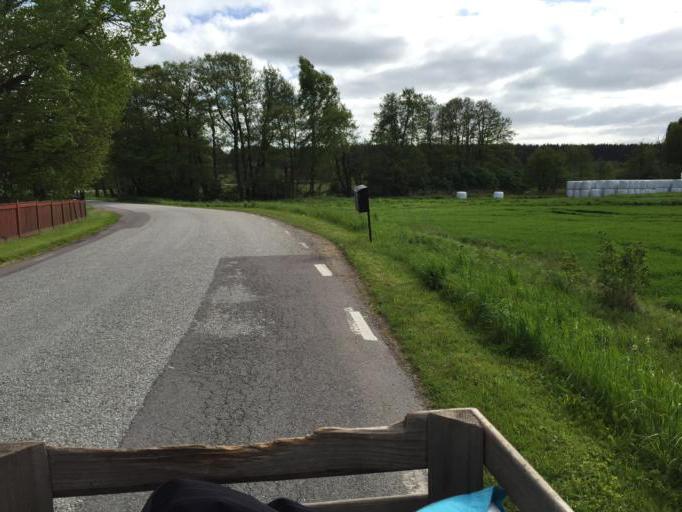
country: SE
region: Skane
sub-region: Sjobo Kommun
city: Blentarp
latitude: 55.6636
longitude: 13.6178
